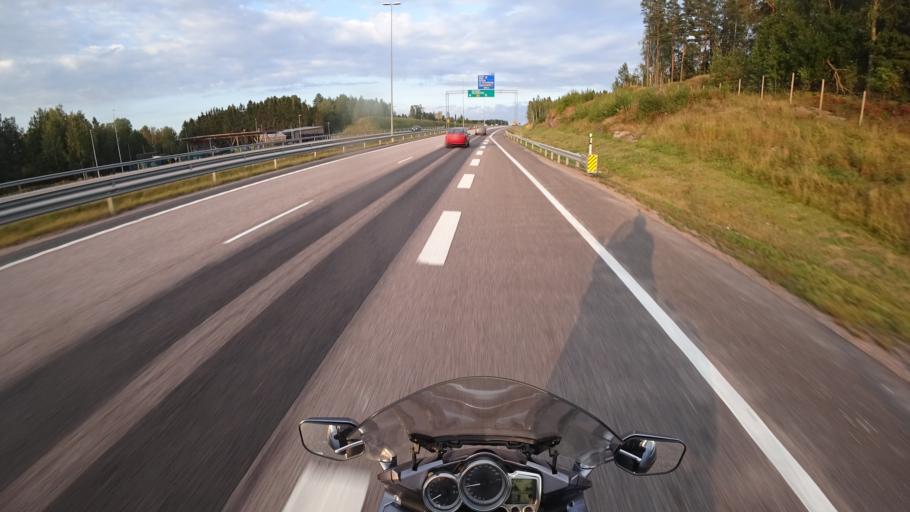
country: FI
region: Uusimaa
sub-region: Helsinki
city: Kirkkonummi
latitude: 60.1353
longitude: 24.5200
